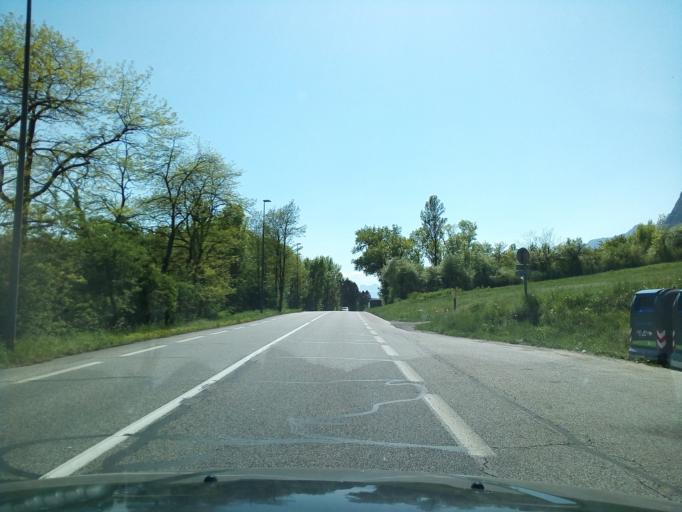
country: FR
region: Rhone-Alpes
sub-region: Departement de l'Isere
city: Saint-Hilaire
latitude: 45.2940
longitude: 5.8952
